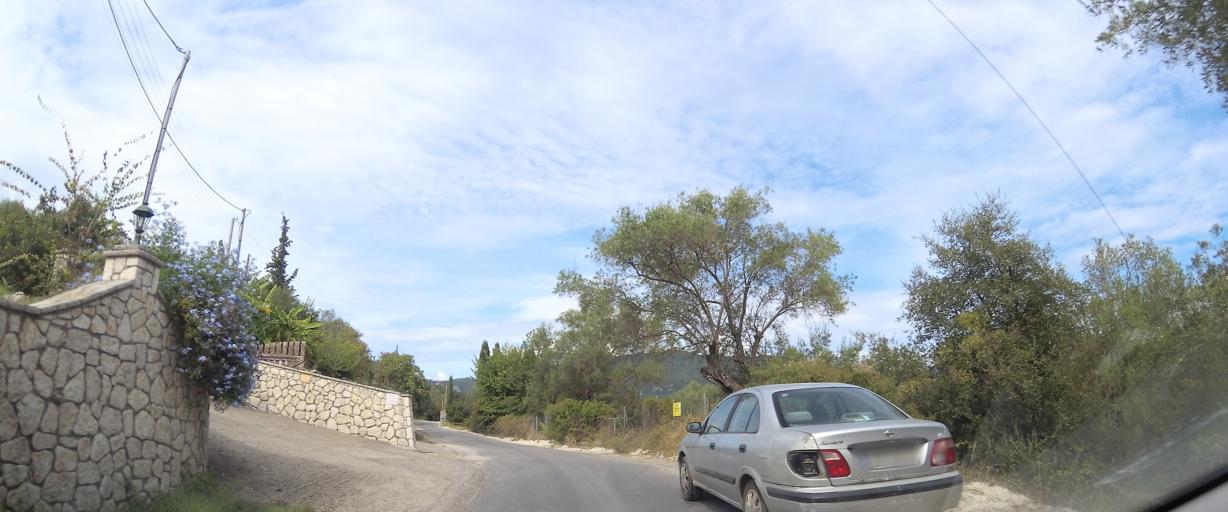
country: GR
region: Ionian Islands
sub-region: Nomos Kerkyras
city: Kontokali
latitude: 39.6909
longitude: 19.8155
